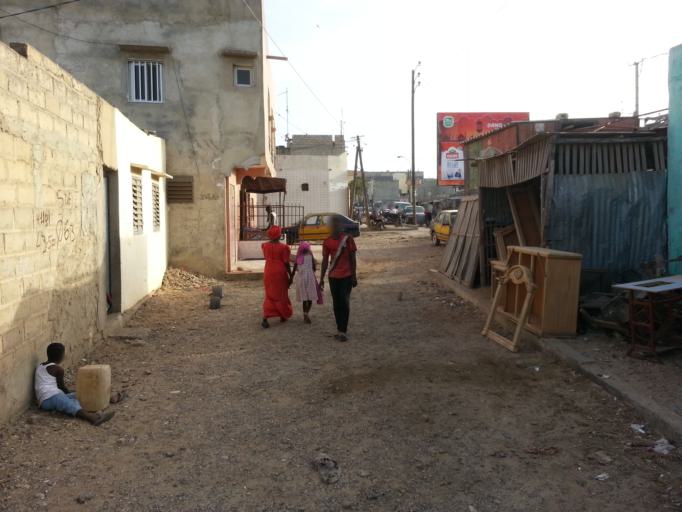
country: SN
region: Dakar
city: Pikine
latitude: 14.7648
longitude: -17.3861
